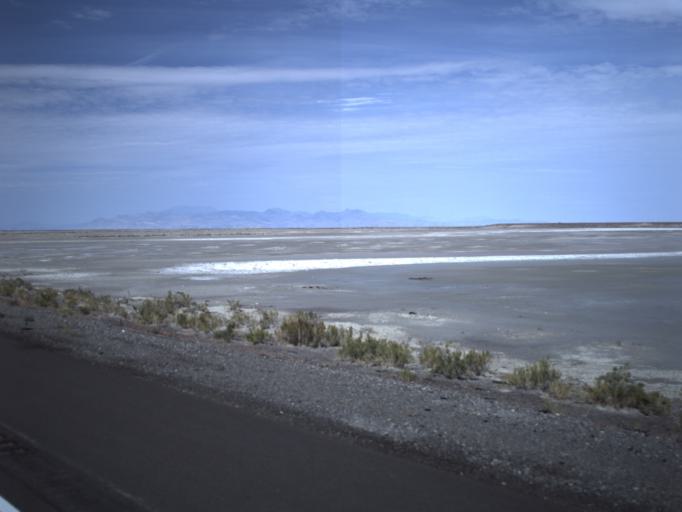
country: US
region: Utah
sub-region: Tooele County
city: Wendover
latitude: 40.7286
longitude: -113.3464
